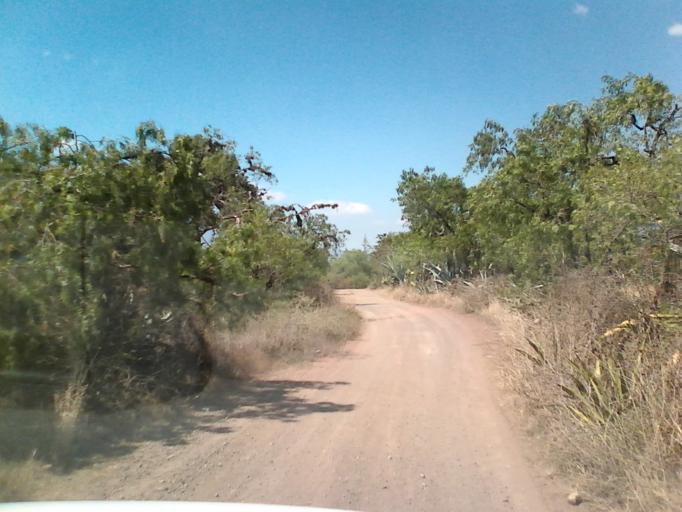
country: CO
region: Boyaca
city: Sachica
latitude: 5.6083
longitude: -73.5578
